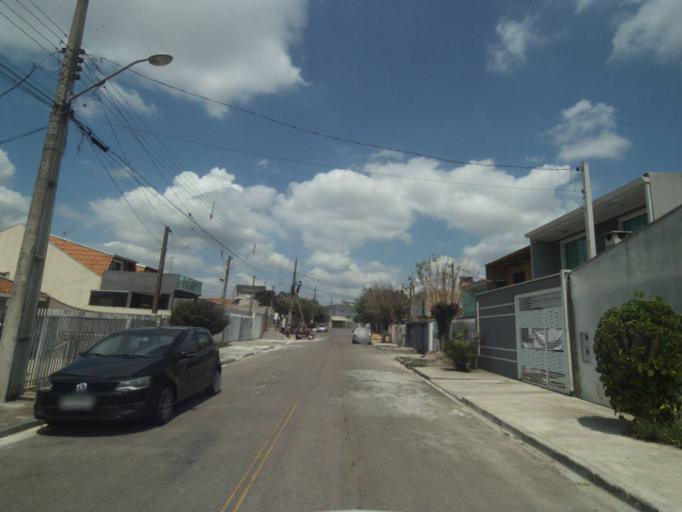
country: BR
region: Parana
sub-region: Sao Jose Dos Pinhais
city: Sao Jose dos Pinhais
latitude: -25.5377
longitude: -49.2524
